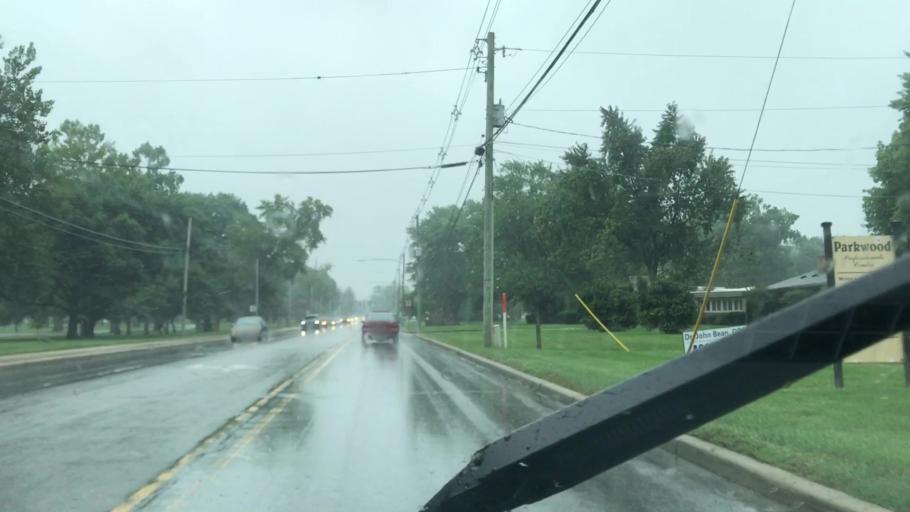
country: US
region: Indiana
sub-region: Boone County
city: Lebanon
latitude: 40.0603
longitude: -86.4715
